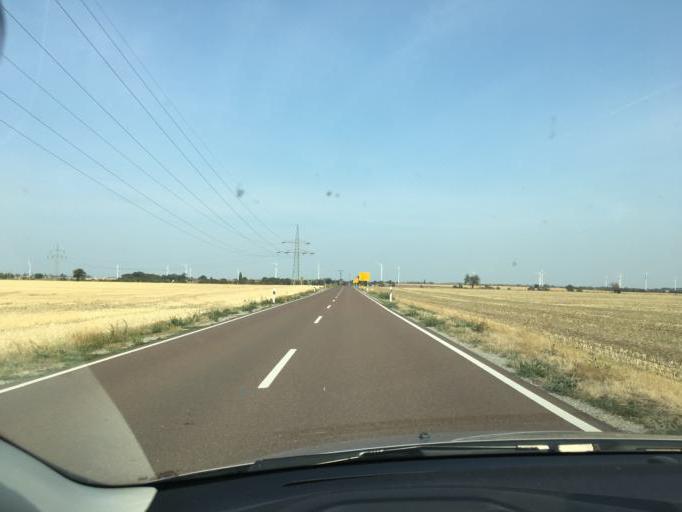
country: DE
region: Saxony-Anhalt
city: Baalberge
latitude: 51.8071
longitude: 11.8384
